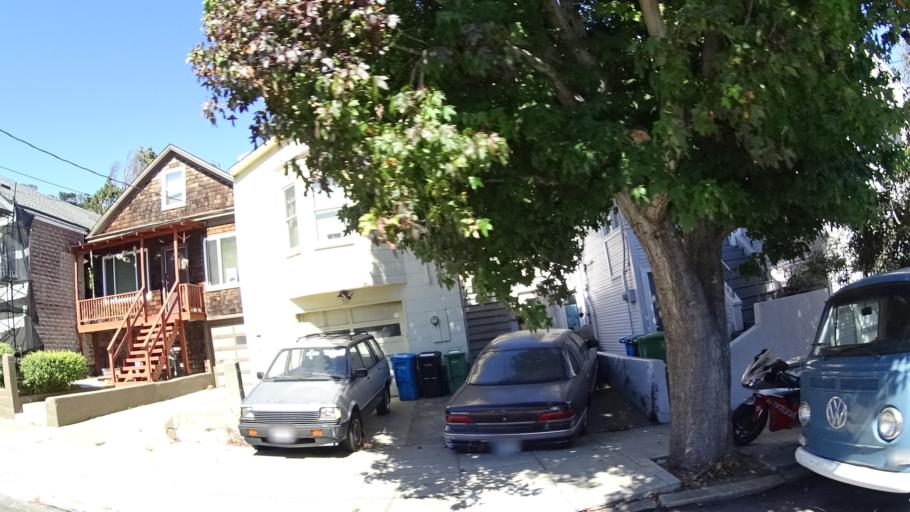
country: US
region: California
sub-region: San Francisco County
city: San Francisco
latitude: 37.7364
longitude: -122.4184
